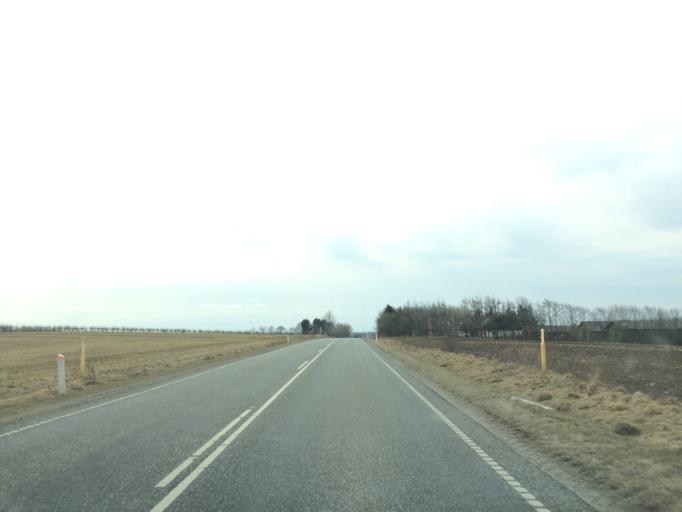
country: DK
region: Central Jutland
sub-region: Ringkobing-Skjern Kommune
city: Videbaek
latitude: 56.0818
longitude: 8.5071
